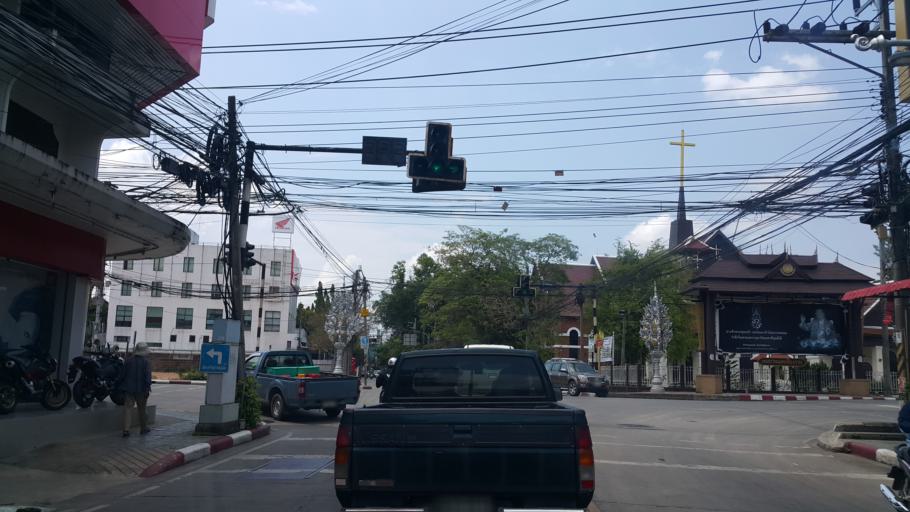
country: TH
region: Chiang Rai
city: Chiang Rai
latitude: 19.9066
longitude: 99.8333
